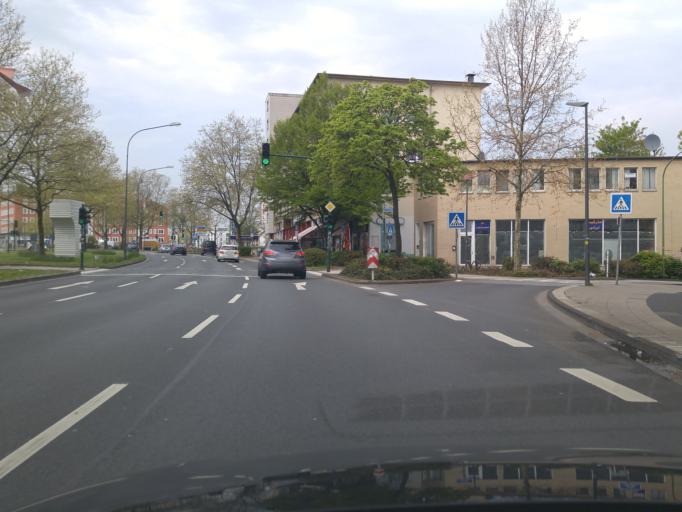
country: DE
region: North Rhine-Westphalia
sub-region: Regierungsbezirk Dusseldorf
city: Essen
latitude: 51.4622
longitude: 7.0142
